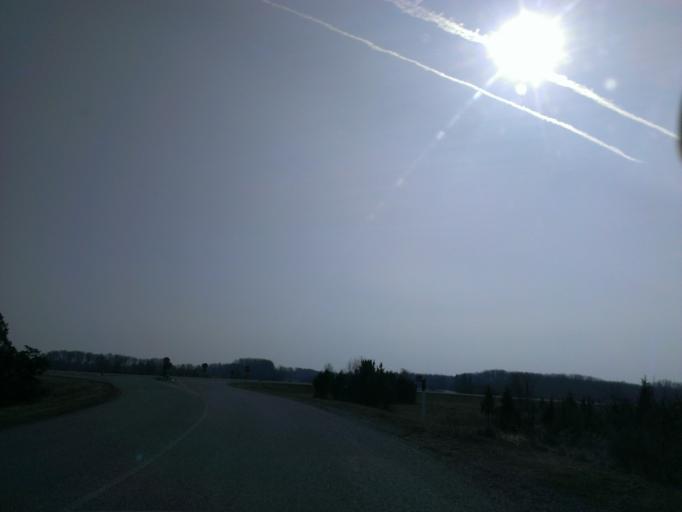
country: EE
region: Saare
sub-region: Orissaare vald
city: Orissaare
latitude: 58.5389
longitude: 23.1106
